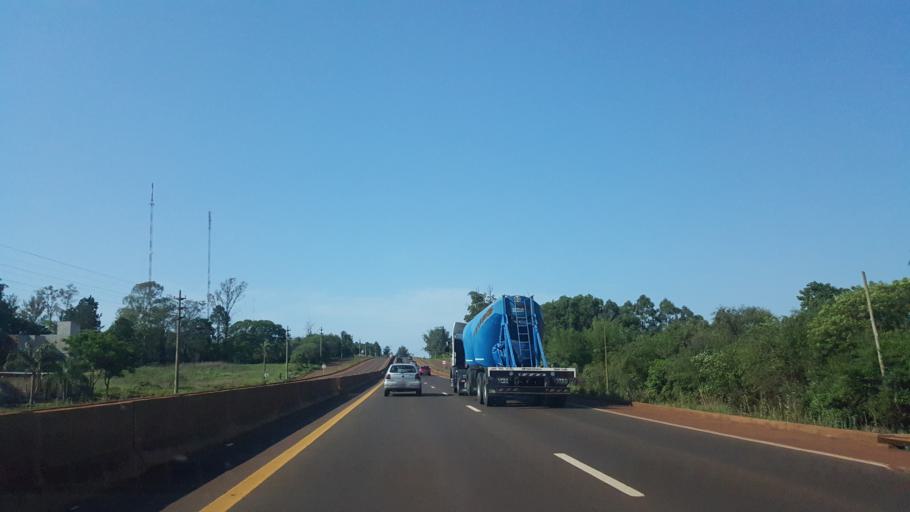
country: AR
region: Misiones
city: Garupa
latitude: -27.4725
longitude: -55.8633
